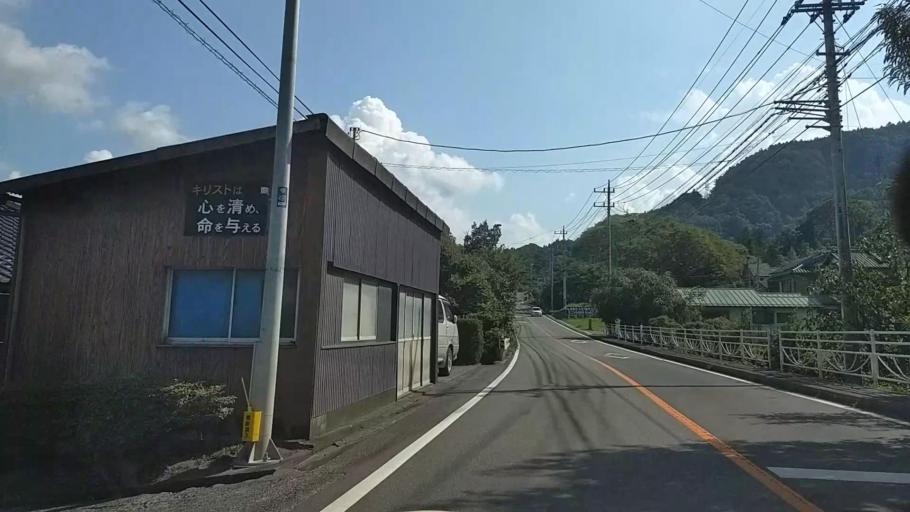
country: JP
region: Yamanashi
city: Ryuo
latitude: 35.4063
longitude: 138.4419
